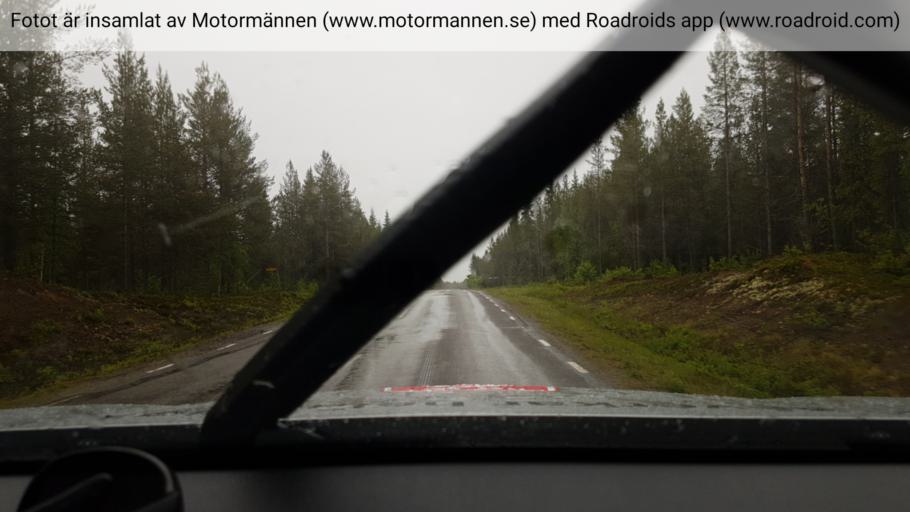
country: SE
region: Vaesterbotten
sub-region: Sorsele Kommun
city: Sorsele
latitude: 65.5986
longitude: 17.4967
